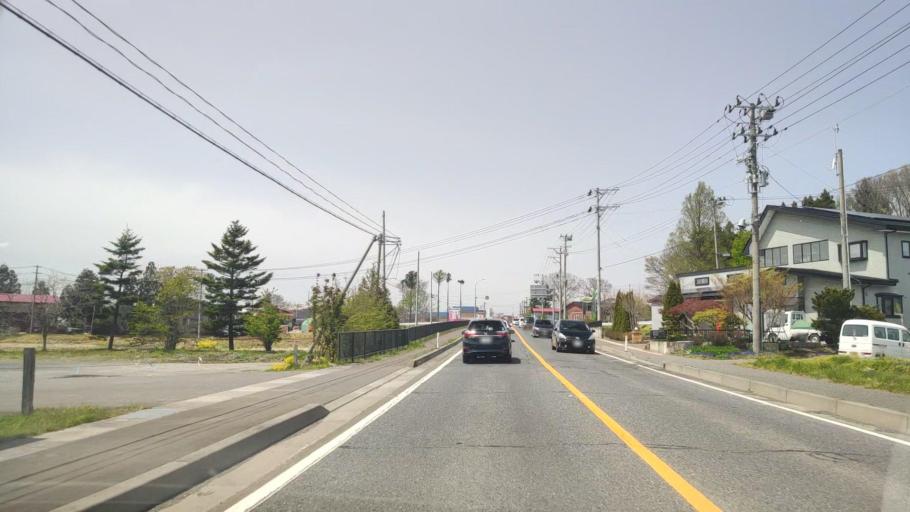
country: JP
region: Aomori
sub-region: Misawa Shi
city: Inuotose
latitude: 40.6059
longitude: 141.2911
